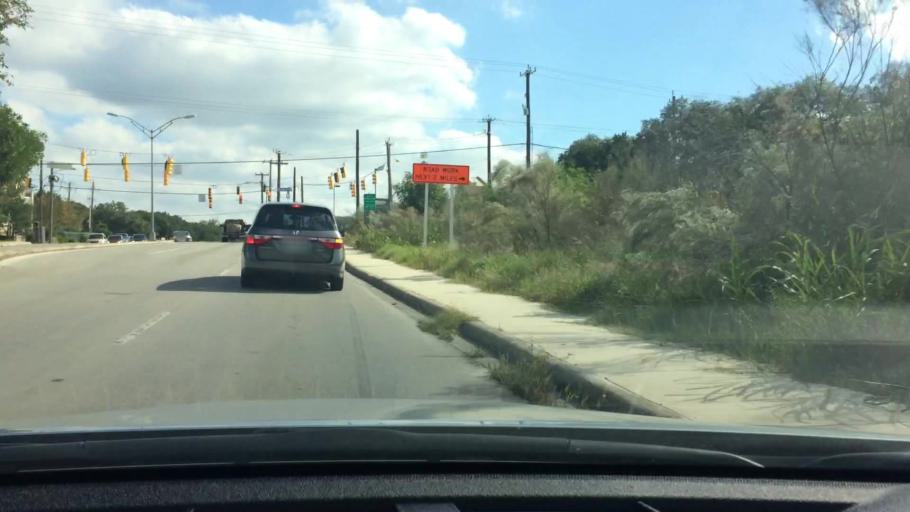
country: US
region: Texas
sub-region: Bexar County
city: Shavano Park
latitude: 29.5776
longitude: -98.5652
